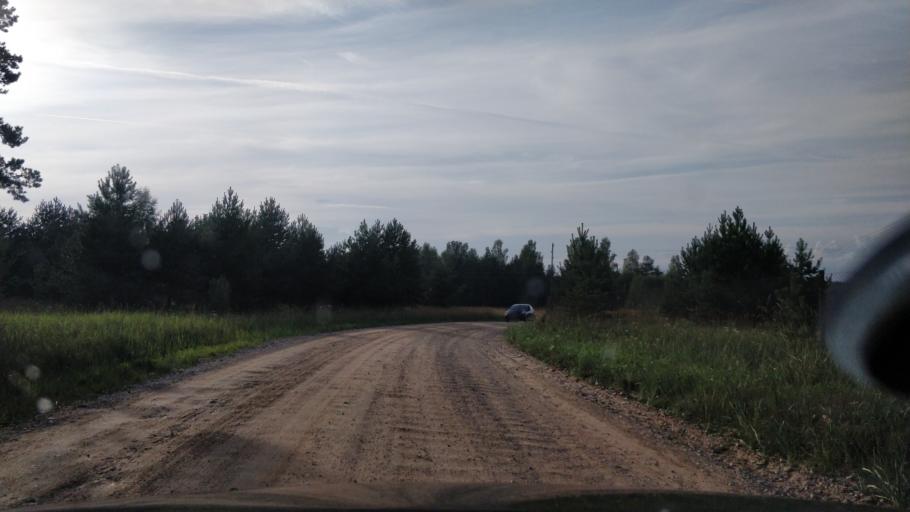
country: LV
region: Incukalns
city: Incukalns
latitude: 57.0944
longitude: 24.7608
